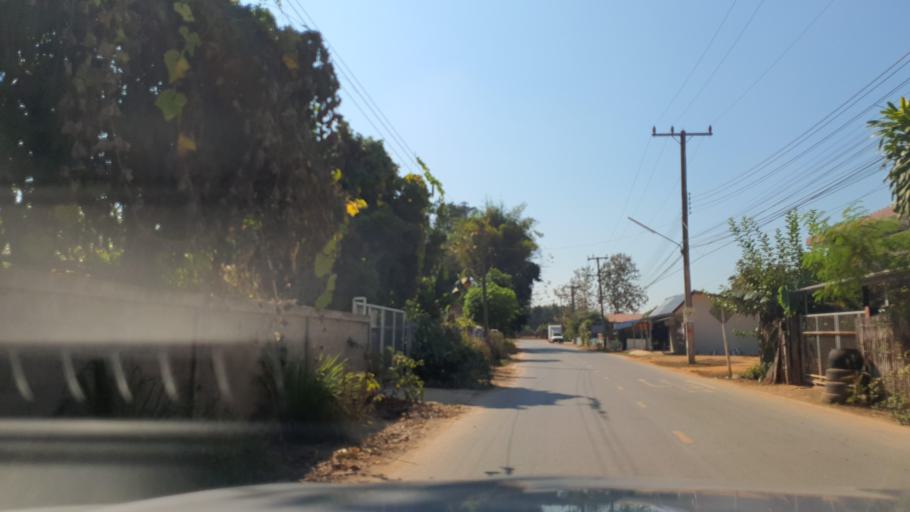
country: TH
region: Nan
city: Pua
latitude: 19.1434
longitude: 100.9243
